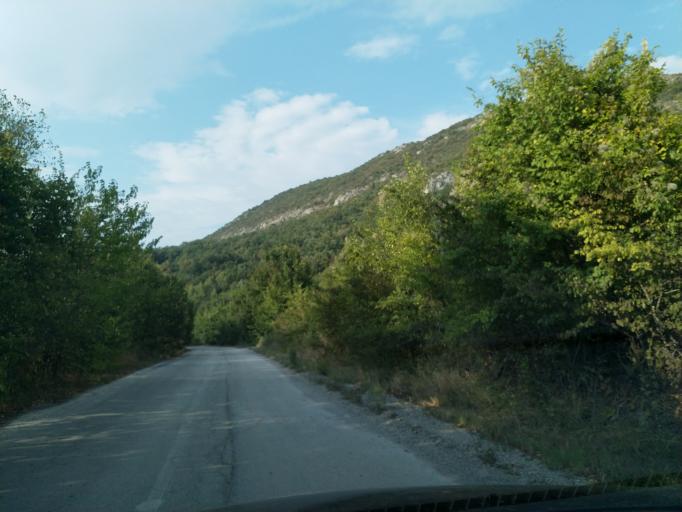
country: RS
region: Central Serbia
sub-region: Pomoravski Okrug
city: Paracin
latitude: 43.8391
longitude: 21.5388
